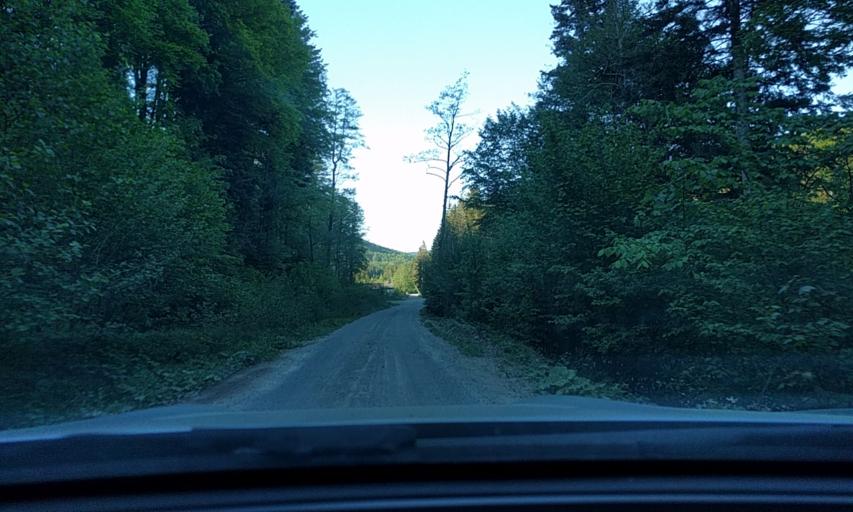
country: RO
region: Bacau
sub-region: Comuna Oituz
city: Ferestrau-Oituz
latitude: 46.1583
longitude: 26.5634
